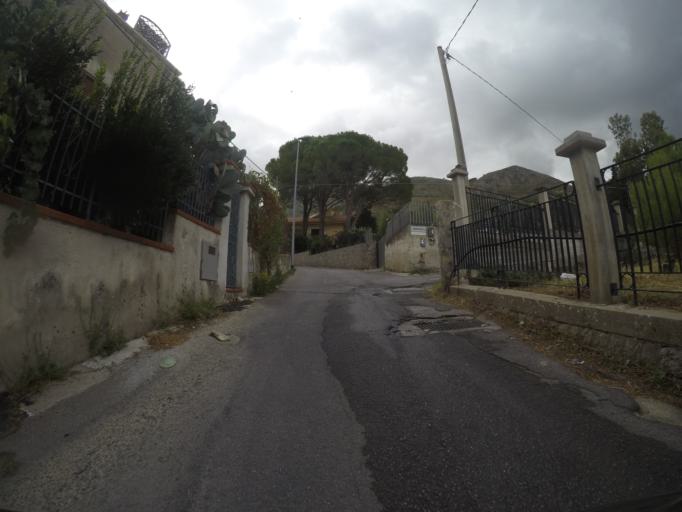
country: IT
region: Sicily
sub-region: Palermo
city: Carini
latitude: 38.1257
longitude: 13.1824
